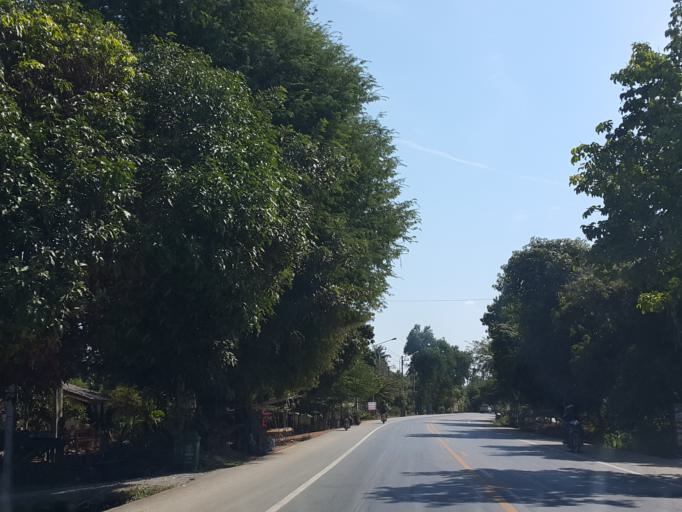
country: TH
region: Sukhothai
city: Sawankhalok
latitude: 17.2547
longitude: 99.8555
